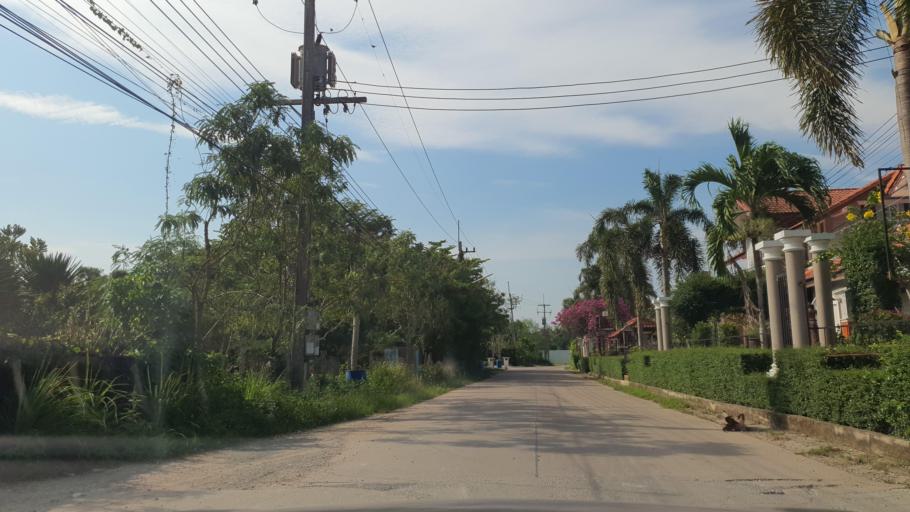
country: TH
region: Chon Buri
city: Sattahip
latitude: 12.7967
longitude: 100.9355
